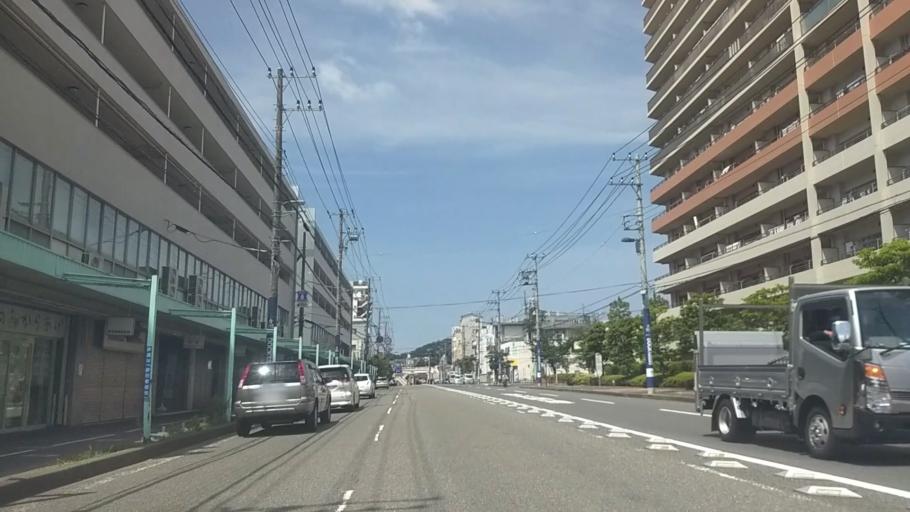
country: JP
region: Kanagawa
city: Yokosuka
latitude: 35.3171
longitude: 139.6338
